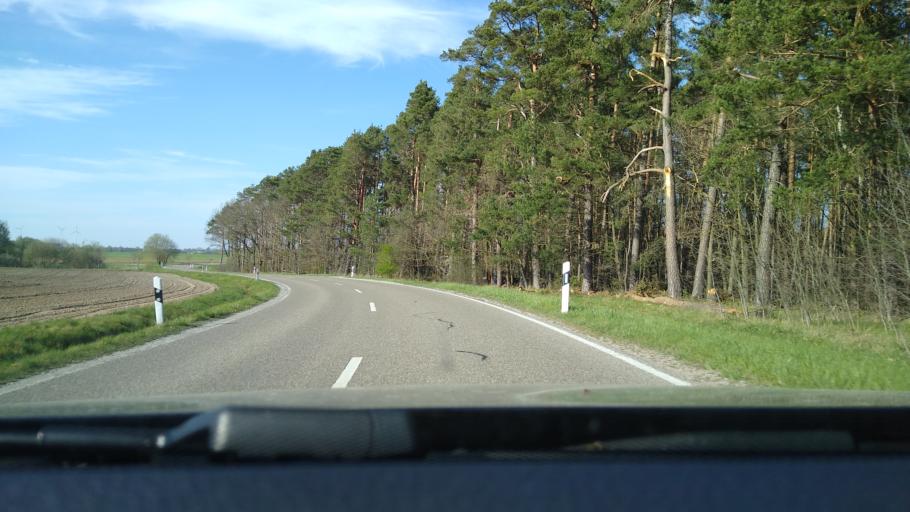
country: DE
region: Bavaria
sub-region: Regierungsbezirk Mittelfranken
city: Merkendorf
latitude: 49.1879
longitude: 10.7226
